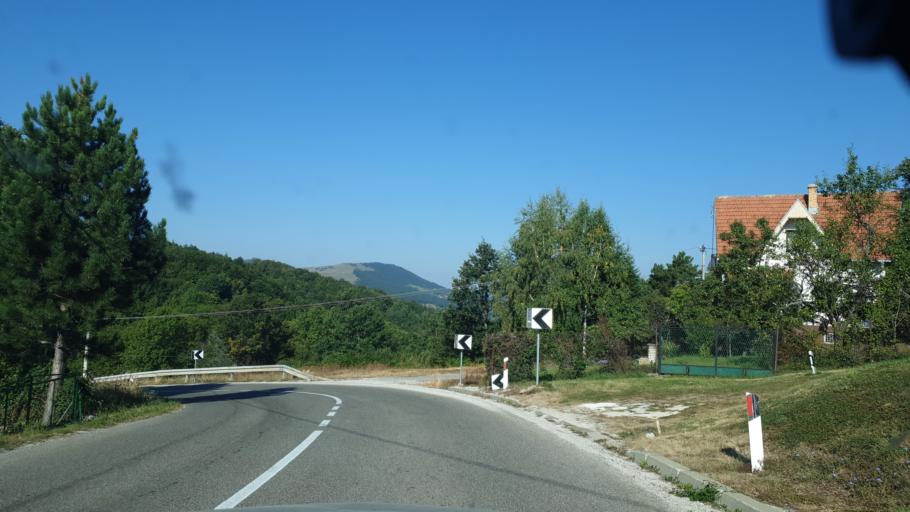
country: RS
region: Central Serbia
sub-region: Zlatiborski Okrug
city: Cajetina
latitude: 43.7260
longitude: 19.8073
